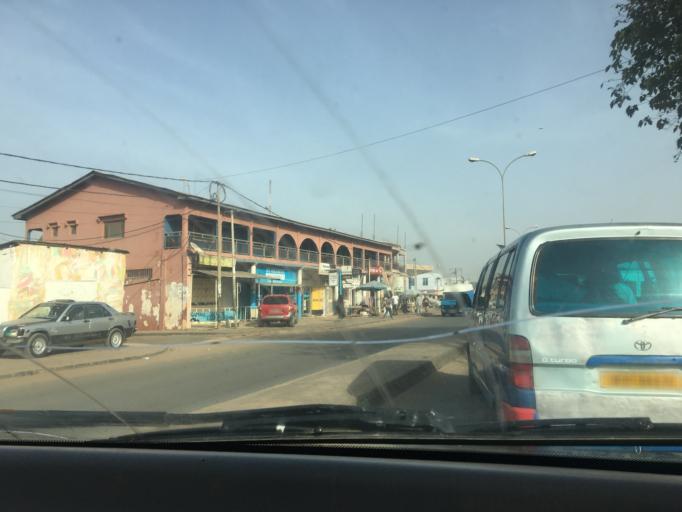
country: GM
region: Western
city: Abuko
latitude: 13.4127
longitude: -16.6711
